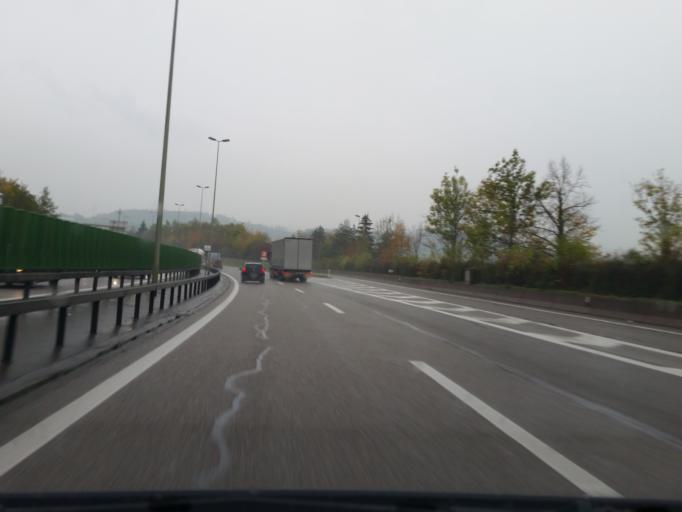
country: CH
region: Zurich
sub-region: Bezirk Winterthur
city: Veltheim (Kreis 5) / Rosenberg
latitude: 47.5251
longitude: 8.7068
